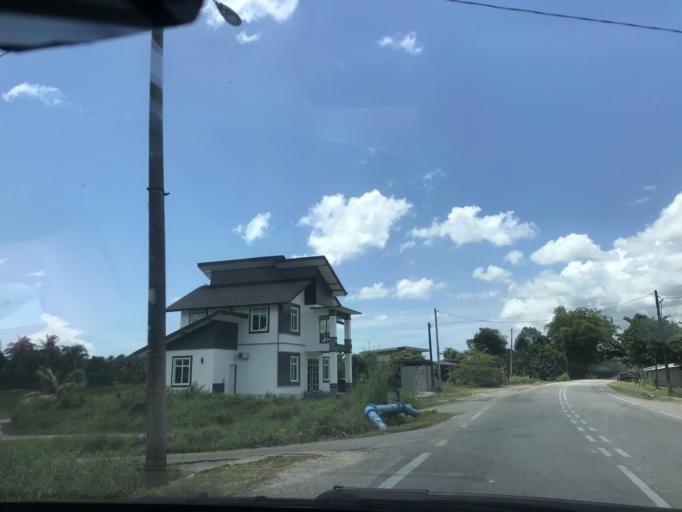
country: MY
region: Kelantan
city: Tumpat
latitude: 6.2080
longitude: 102.1134
